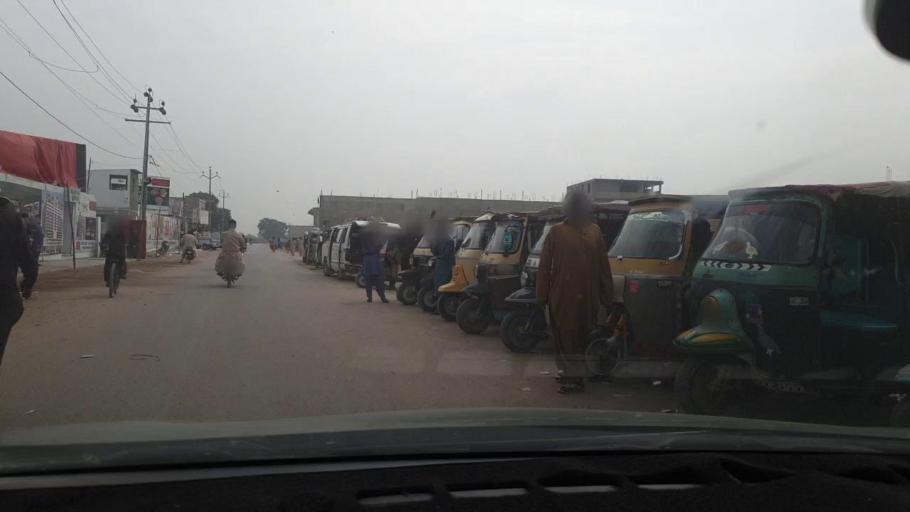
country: PK
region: Sindh
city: Malir Cantonment
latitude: 24.9195
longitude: 67.2580
